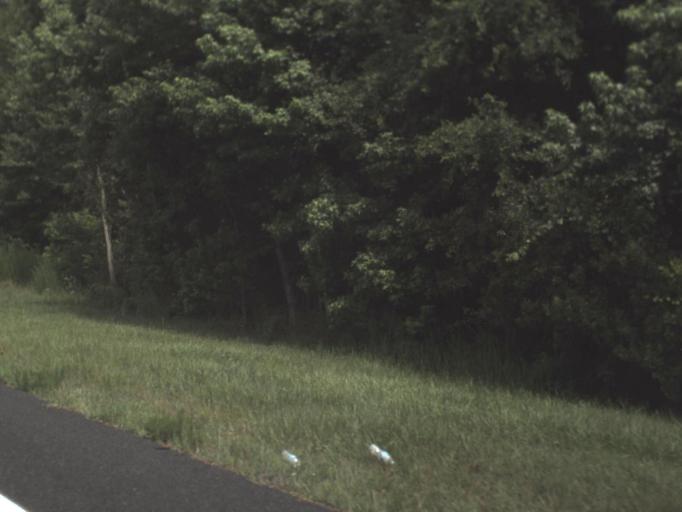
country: US
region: Florida
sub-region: Alachua County
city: Gainesville
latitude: 29.6074
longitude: -82.2282
